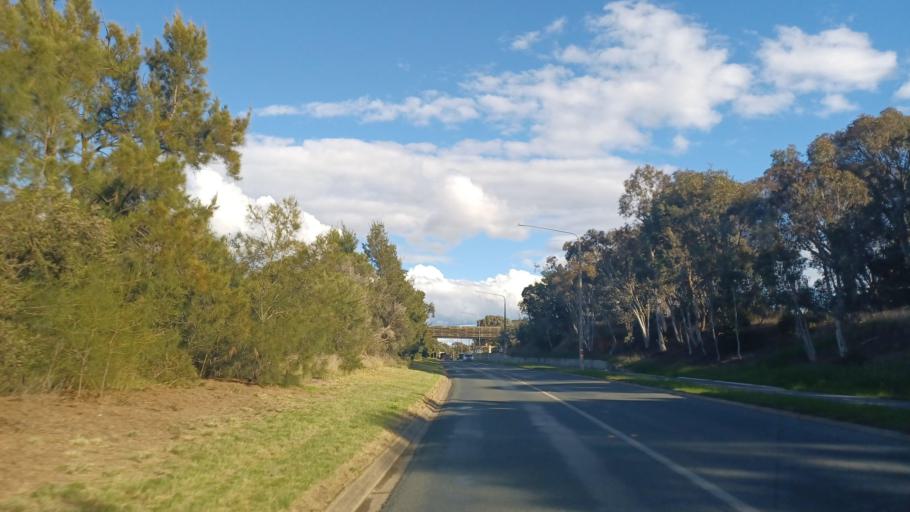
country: AU
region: Australian Capital Territory
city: Belconnen
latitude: -35.1872
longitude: 149.0723
